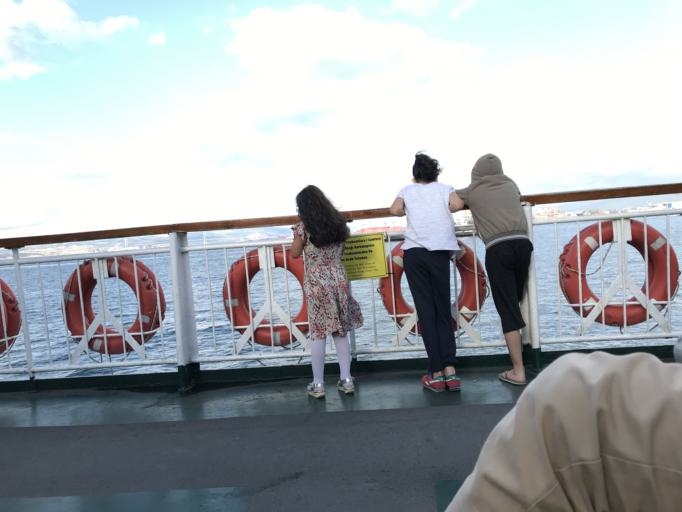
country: TR
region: Yalova
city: Taskopru
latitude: 40.7084
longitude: 29.4310
